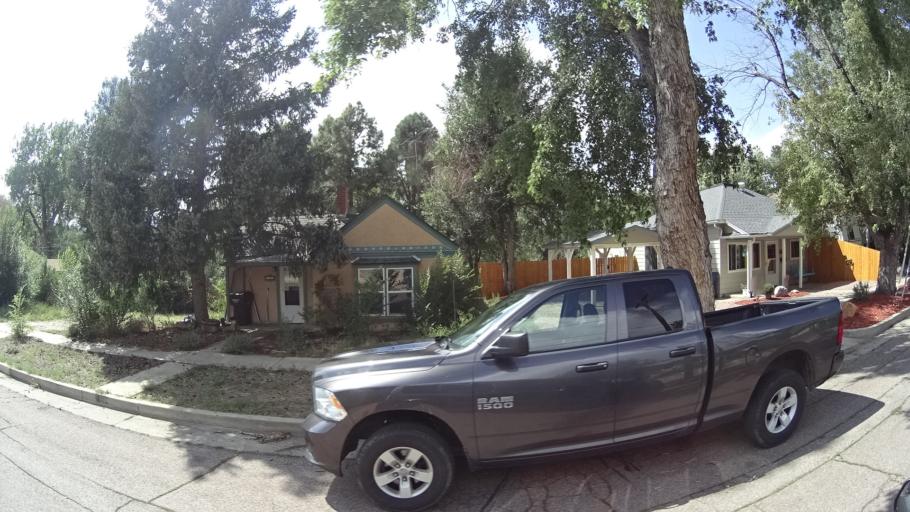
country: US
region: Colorado
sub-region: El Paso County
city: Colorado Springs
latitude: 38.8453
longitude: -104.8102
